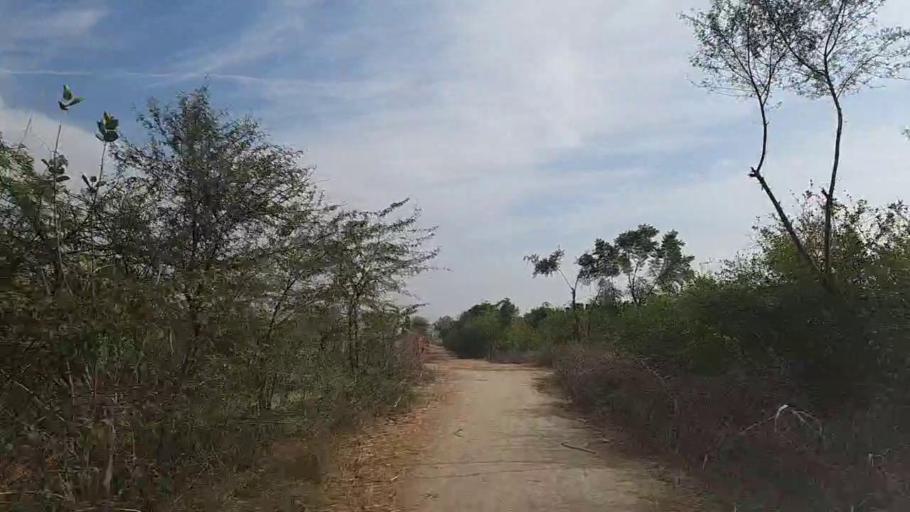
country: PK
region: Sindh
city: Daur
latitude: 26.5197
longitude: 68.4172
